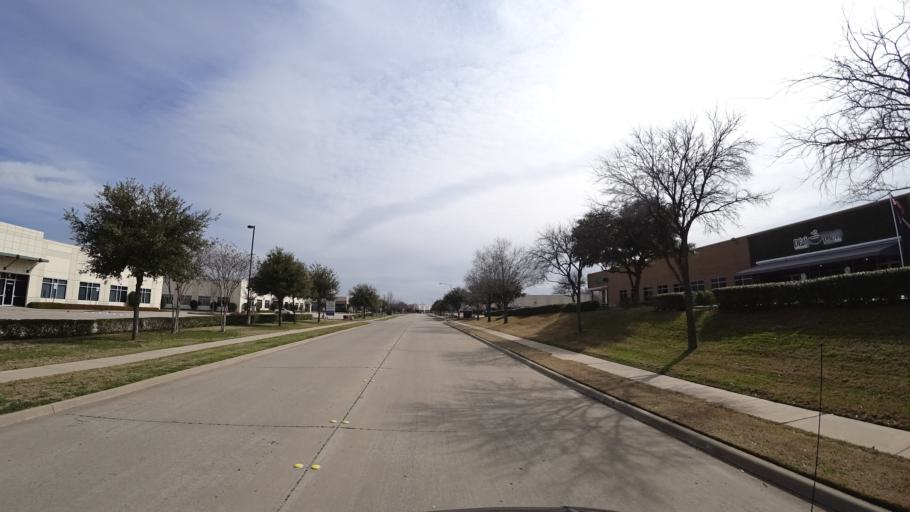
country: US
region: Texas
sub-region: Denton County
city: Lewisville
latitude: 33.0197
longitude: -96.9772
